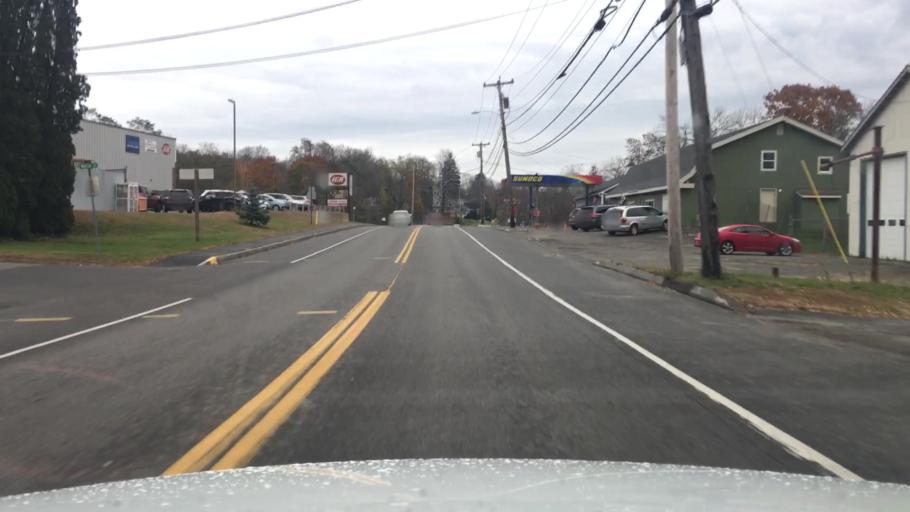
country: US
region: Maine
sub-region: Kennebec County
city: Randolph
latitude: 44.2293
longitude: -69.7661
